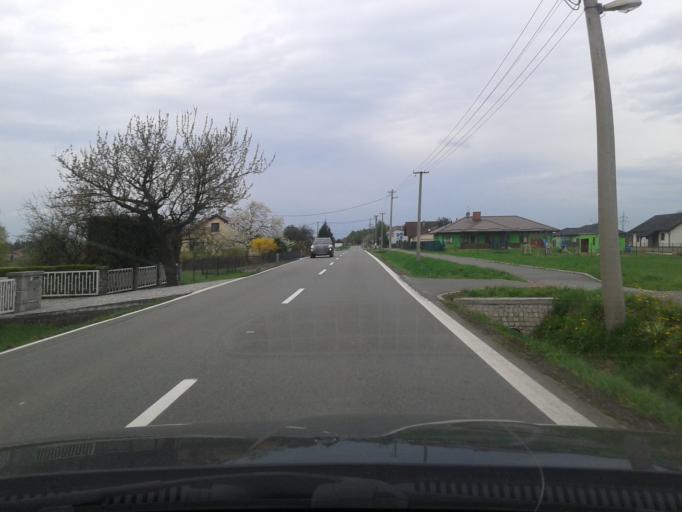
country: CZ
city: Sedliste
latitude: 49.7255
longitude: 18.3666
